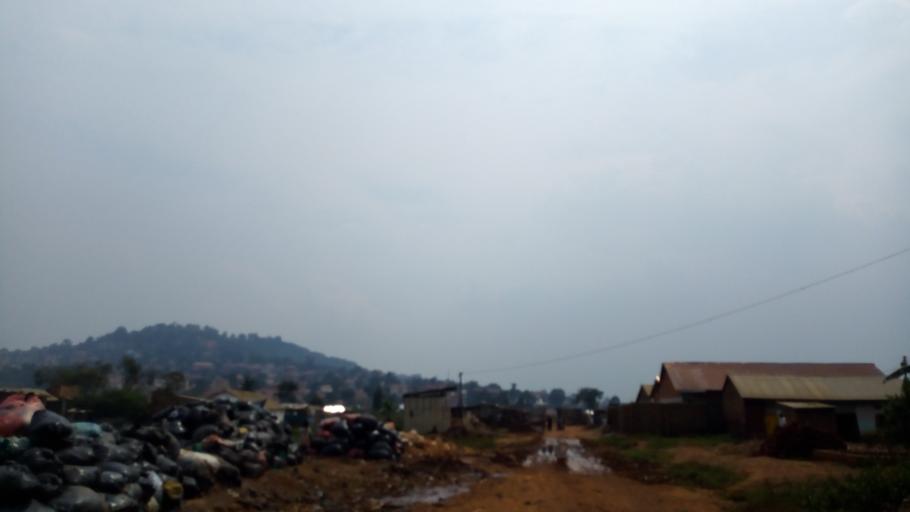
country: UG
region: Central Region
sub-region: Wakiso District
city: Kireka
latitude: 0.3276
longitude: 32.6441
